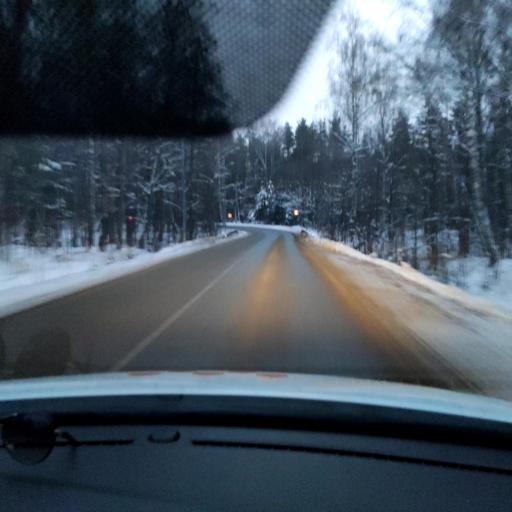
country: RU
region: Tatarstan
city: Vysokaya Gora
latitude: 55.9303
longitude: 49.1579
